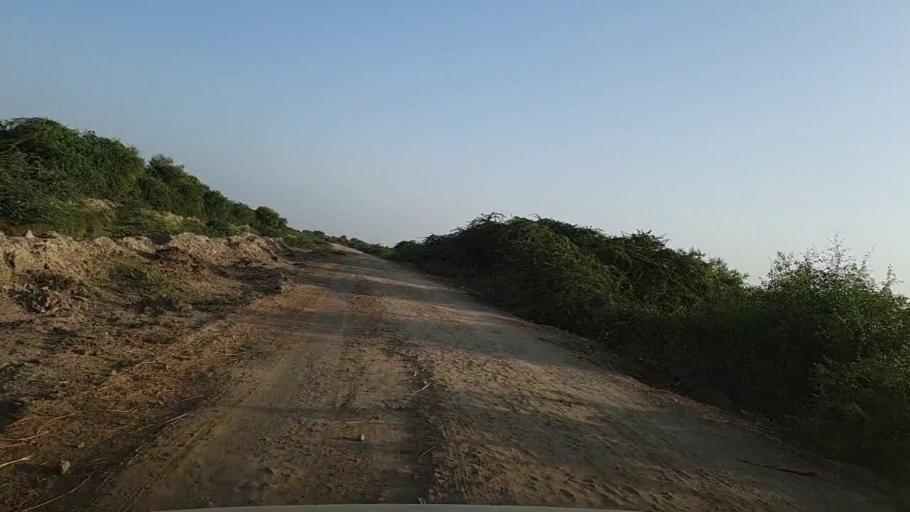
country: PK
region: Sindh
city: Kario
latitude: 24.7081
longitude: 68.6667
